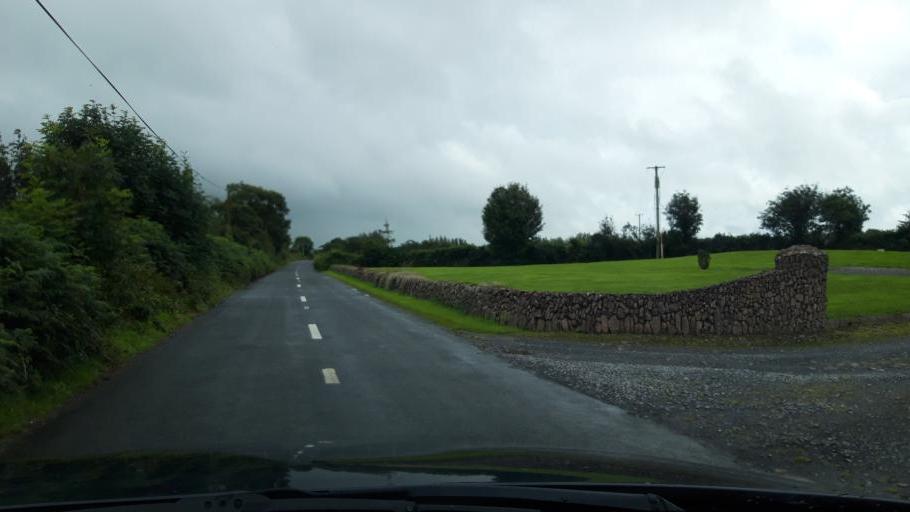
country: IE
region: Munster
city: Cahir
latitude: 52.1706
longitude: -7.8602
